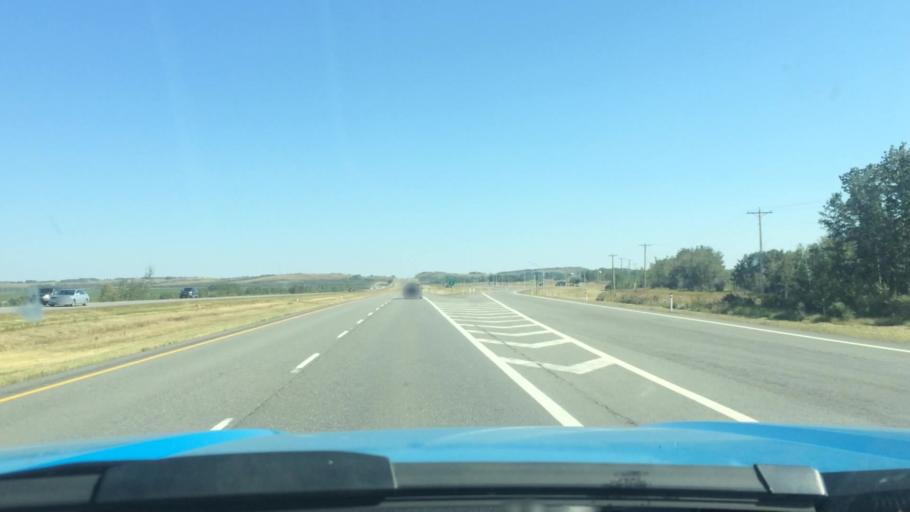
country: CA
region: Alberta
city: Cochrane
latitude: 51.1091
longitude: -114.6373
